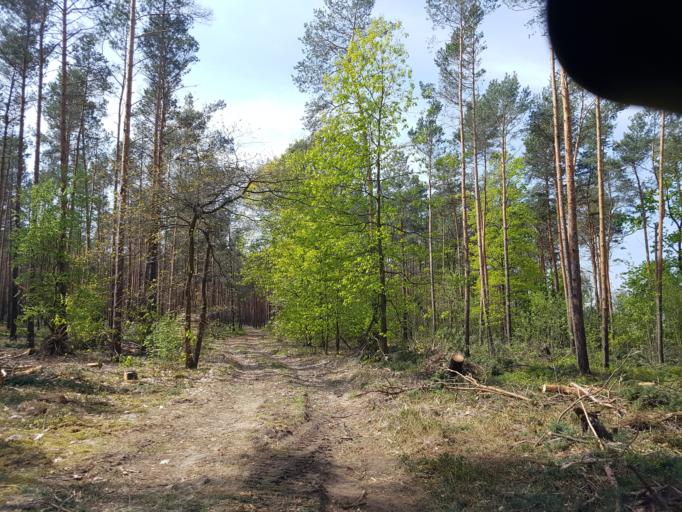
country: DE
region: Brandenburg
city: Finsterwalde
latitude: 51.5764
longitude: 13.6895
